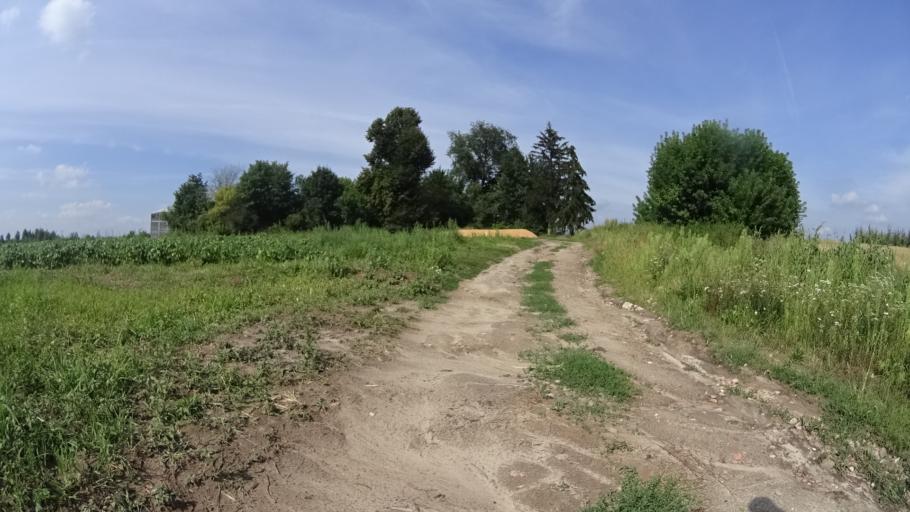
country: PL
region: Masovian Voivodeship
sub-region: Powiat grojecki
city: Goszczyn
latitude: 51.6906
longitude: 20.8390
